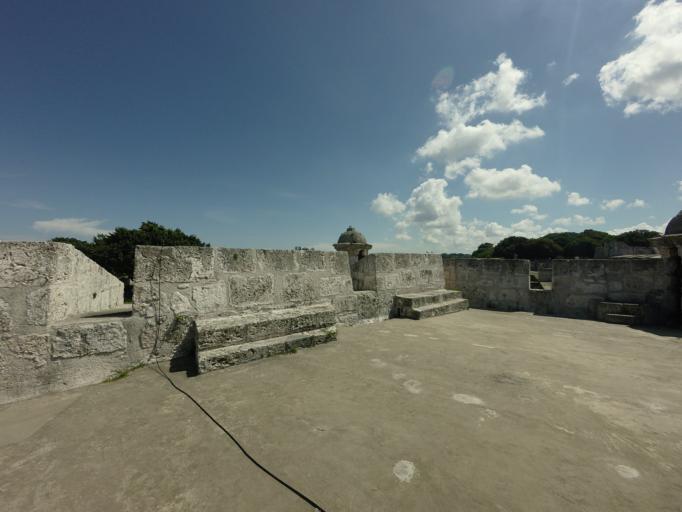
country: CU
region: La Habana
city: Centro Habana
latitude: 23.1480
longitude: -82.3510
